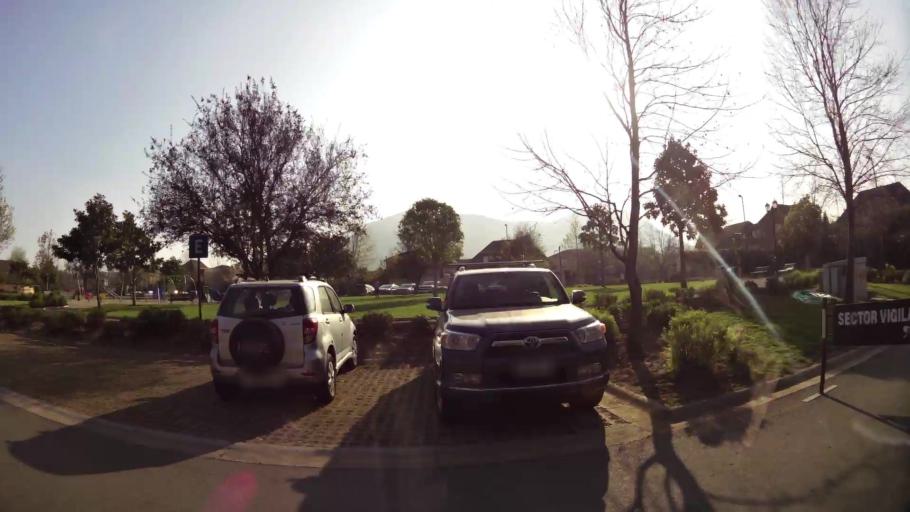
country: CL
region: Santiago Metropolitan
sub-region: Provincia de Santiago
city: Villa Presidente Frei, Nunoa, Santiago, Chile
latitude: -33.3578
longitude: -70.5359
